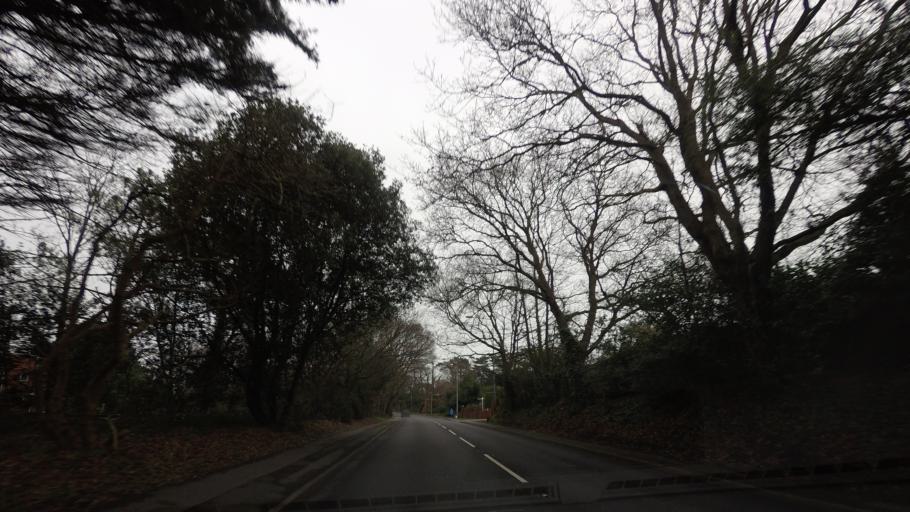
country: GB
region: England
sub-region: East Sussex
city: Bexhill-on-Sea
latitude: 50.8455
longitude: 0.4387
